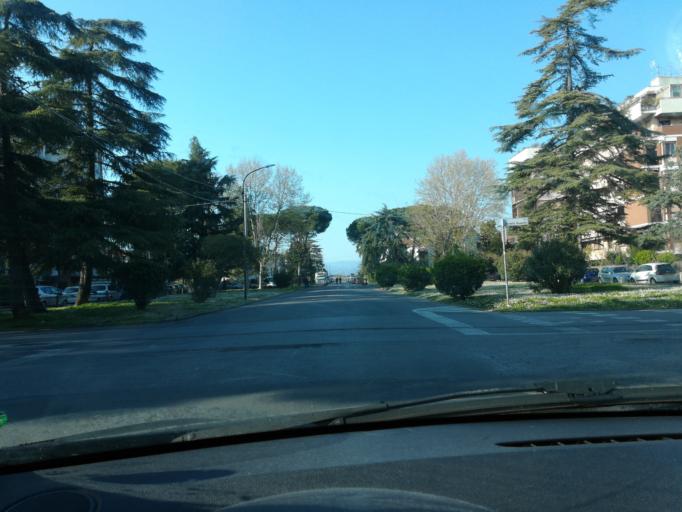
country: IT
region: Tuscany
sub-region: Province of Pisa
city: Pisa
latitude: 43.7321
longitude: 10.4029
